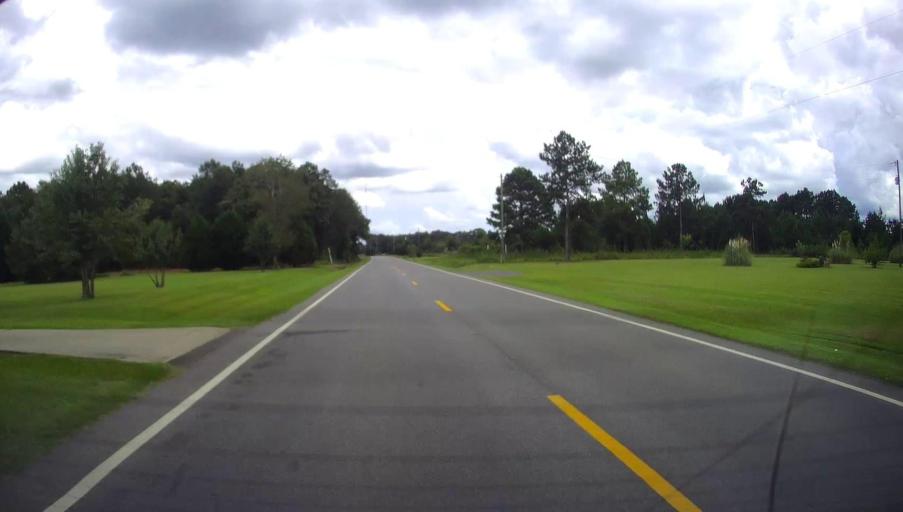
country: US
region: Georgia
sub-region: Macon County
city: Oglethorpe
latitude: 32.2708
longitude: -84.1175
